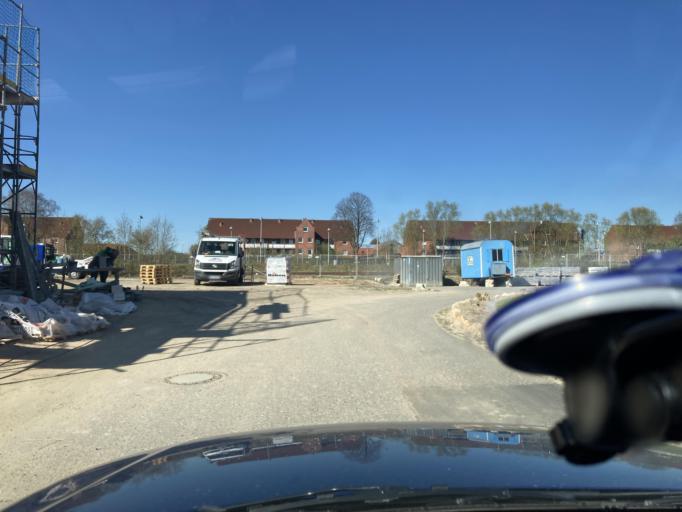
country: DE
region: Schleswig-Holstein
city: Heide
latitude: 54.1907
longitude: 9.1032
